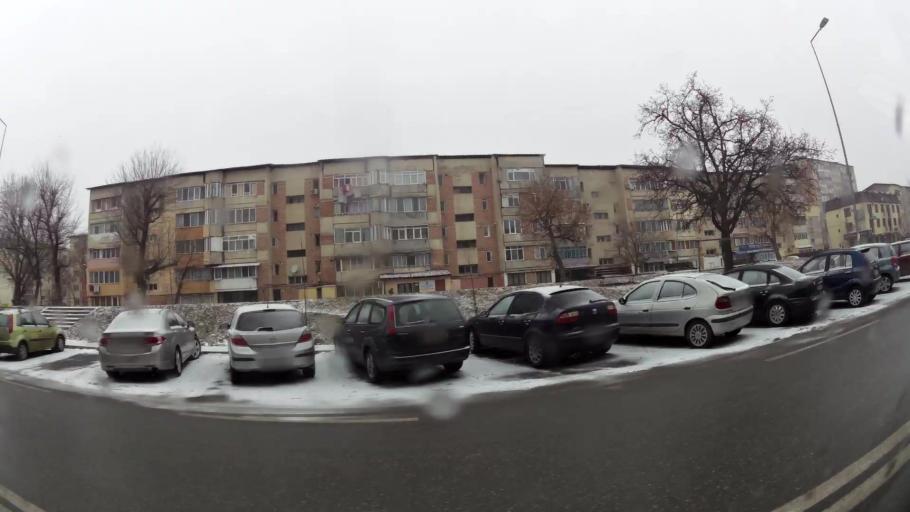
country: RO
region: Dambovita
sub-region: Municipiul Targoviste
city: Targoviste
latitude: 44.9192
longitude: 25.4740
